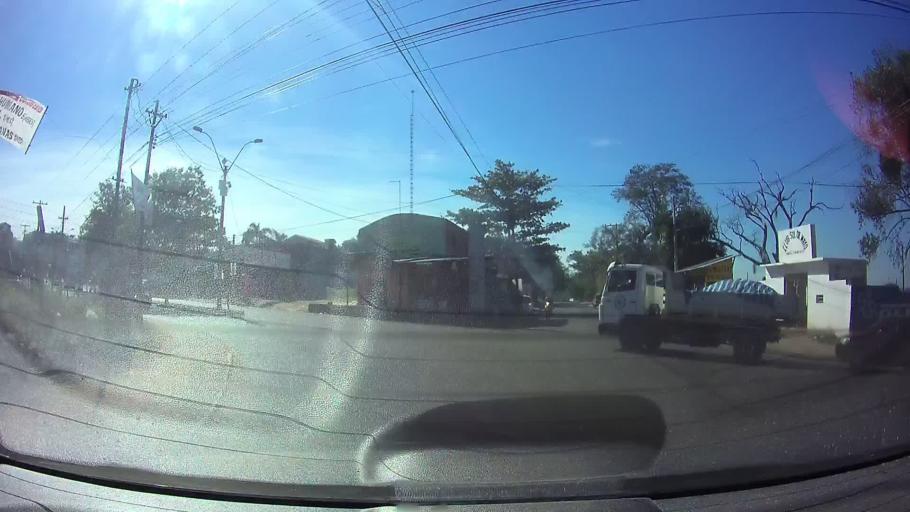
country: PY
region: Central
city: Villa Elisa
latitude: -25.3745
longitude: -57.5791
